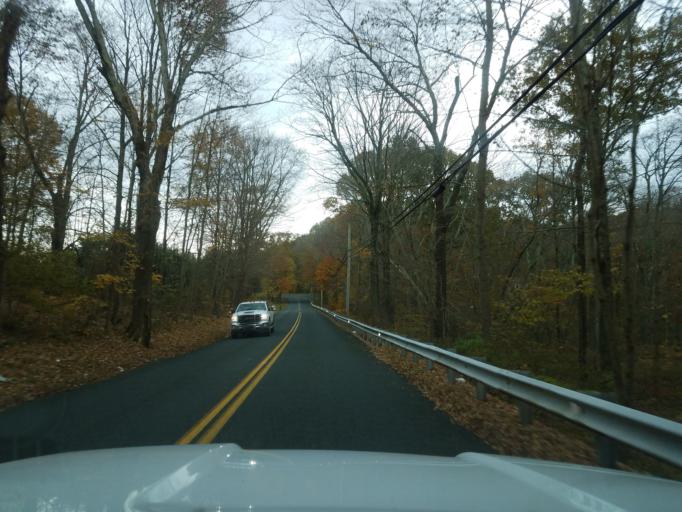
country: US
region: Connecticut
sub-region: New Haven County
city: Middlebury
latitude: 41.5032
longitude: -73.1628
